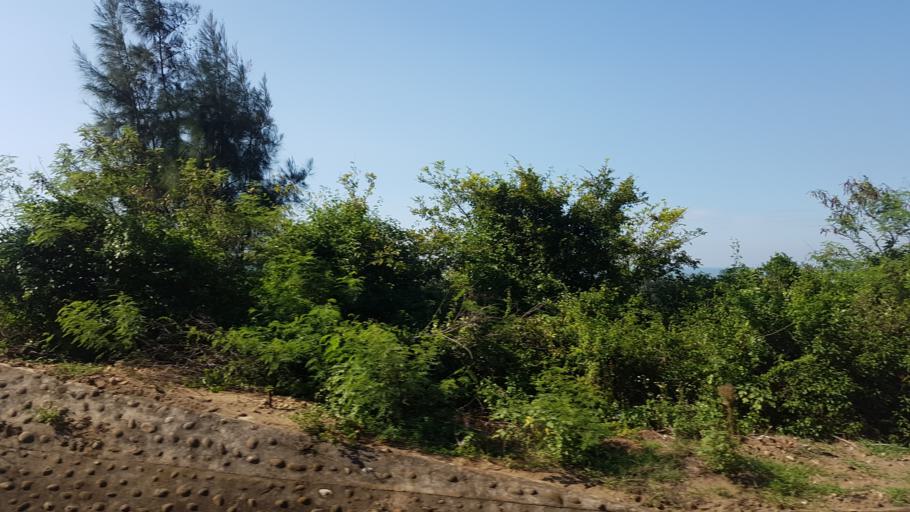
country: TW
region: Taiwan
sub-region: Hsinchu
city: Hsinchu
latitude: 24.7282
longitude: 120.8765
